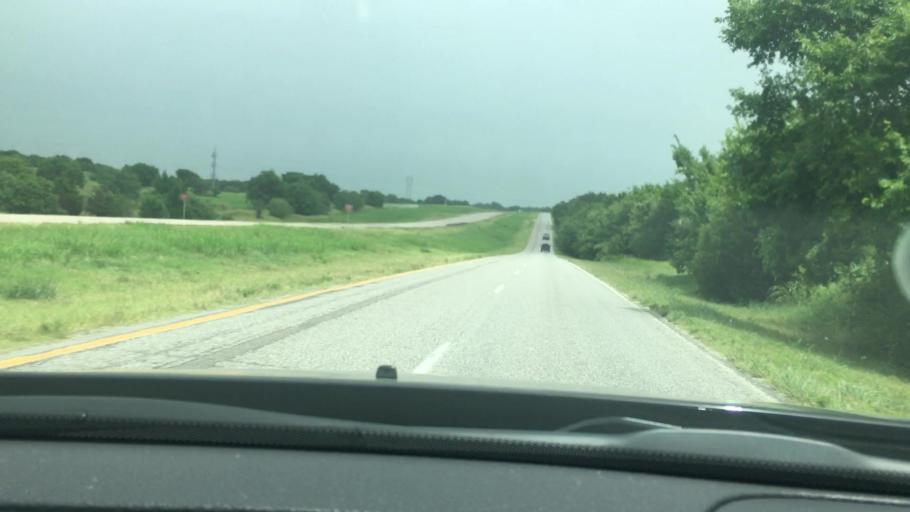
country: US
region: Oklahoma
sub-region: Pontotoc County
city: Ada
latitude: 34.6863
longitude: -96.7573
